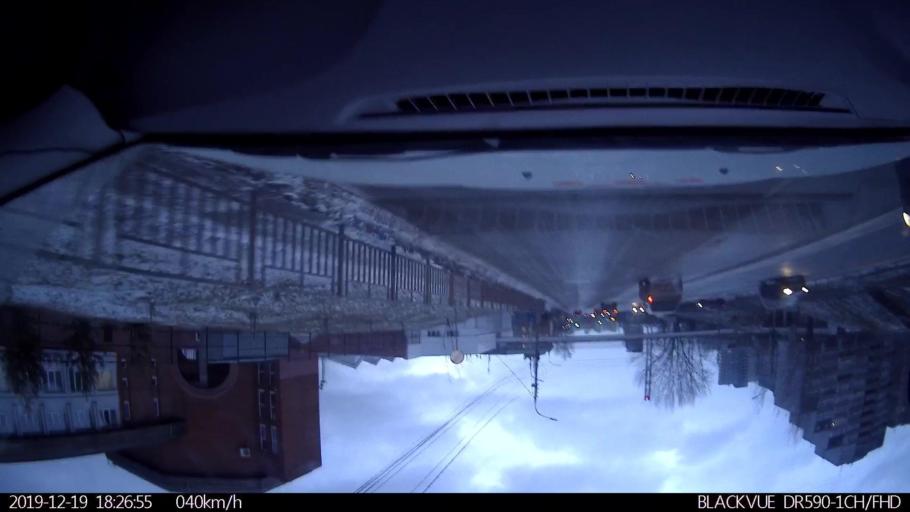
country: RU
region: Nizjnij Novgorod
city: Nizhniy Novgorod
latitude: 56.3418
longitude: 43.9388
